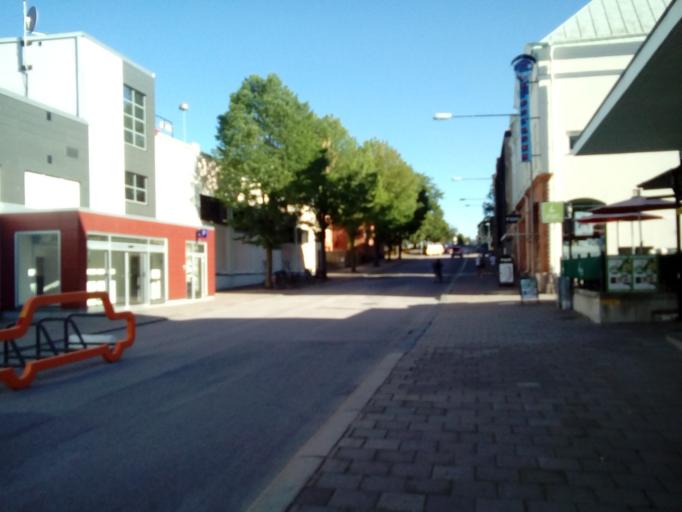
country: SE
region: Kalmar
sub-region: Vasterviks Kommun
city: Vaestervik
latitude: 57.7575
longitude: 16.6393
